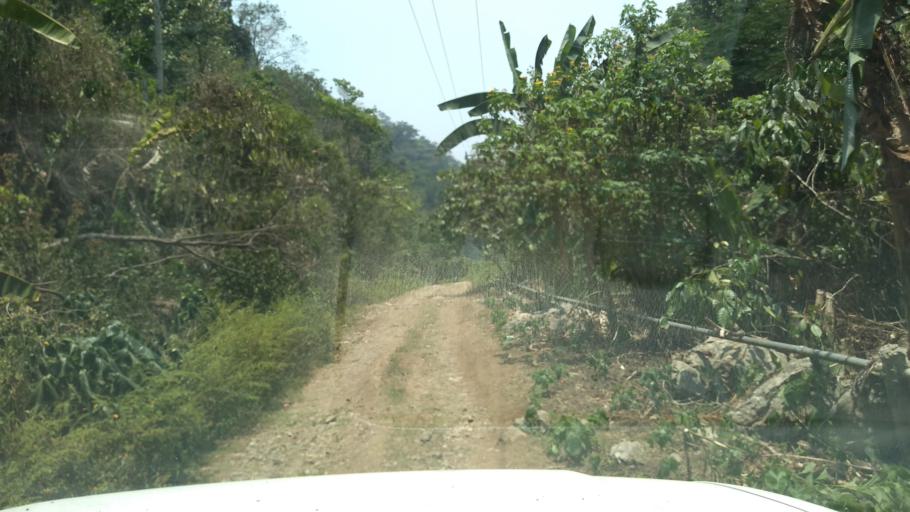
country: MX
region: Veracruz
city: Motzorongo
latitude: 18.5985
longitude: -96.7379
